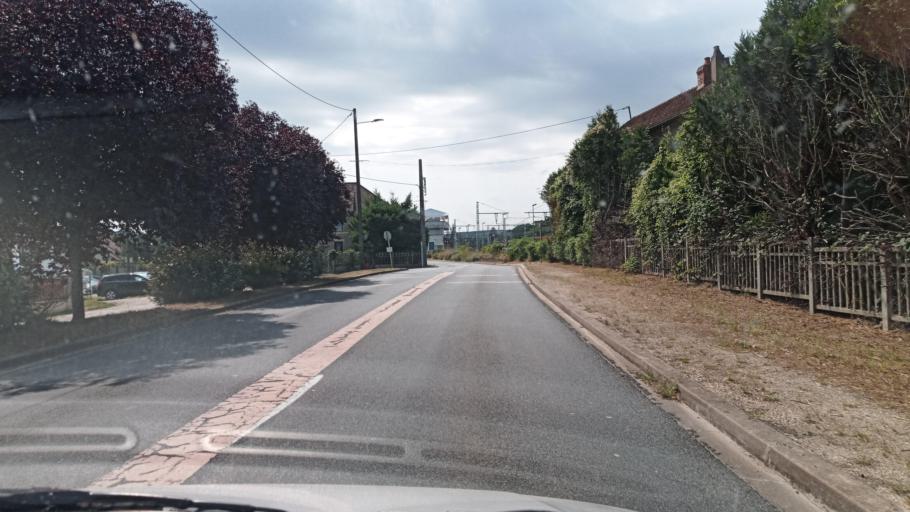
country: FR
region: Bourgogne
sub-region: Departement de l'Yonne
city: Villeneuve-sur-Yonne
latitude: 48.0870
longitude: 3.2868
